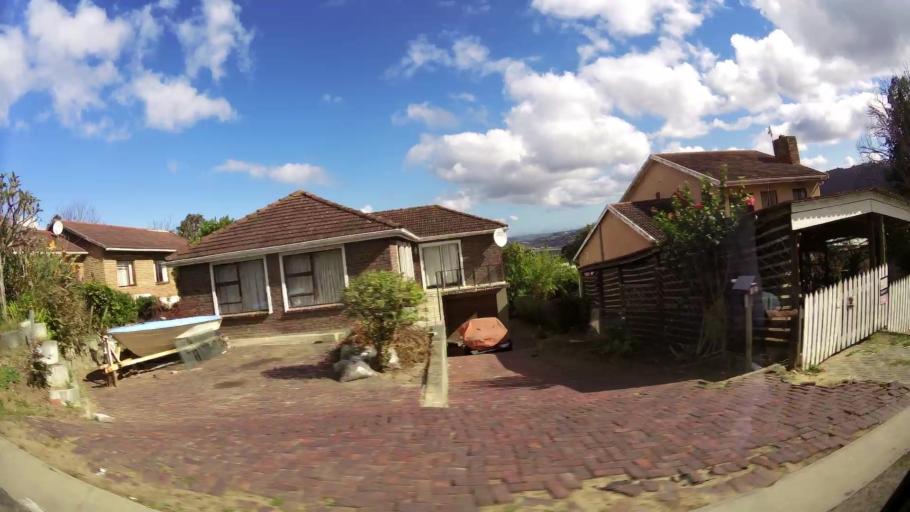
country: ZA
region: Western Cape
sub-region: Eden District Municipality
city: Knysna
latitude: -34.0488
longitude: 23.0827
